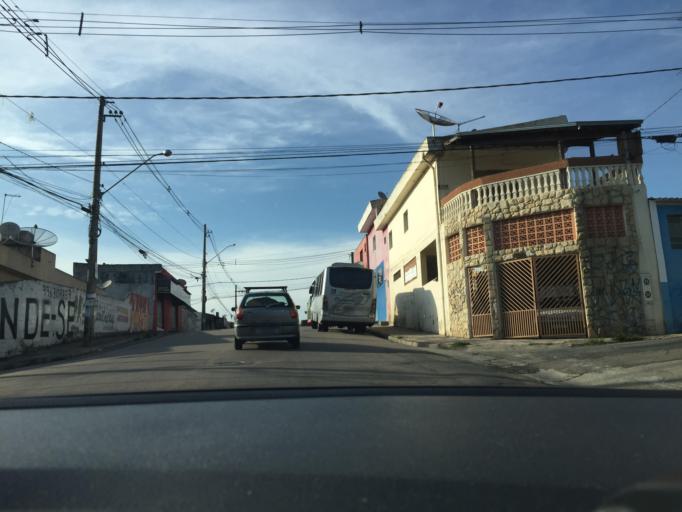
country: BR
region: Sao Paulo
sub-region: Campo Limpo Paulista
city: Campo Limpo Paulista
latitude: -23.2092
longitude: -46.7628
